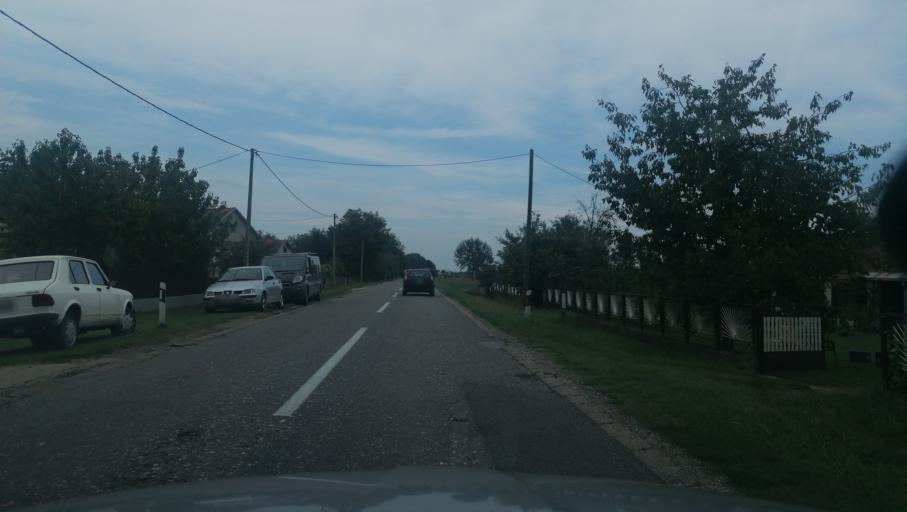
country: RS
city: Klenje
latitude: 44.8207
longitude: 19.4515
